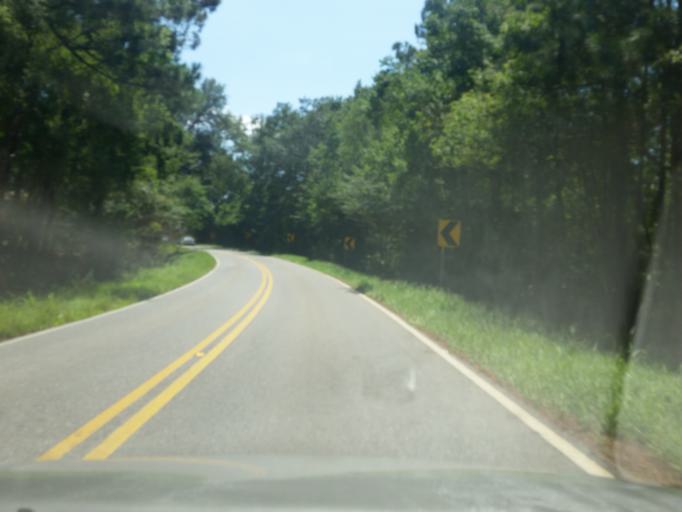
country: US
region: Alabama
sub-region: Baldwin County
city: Robertsdale
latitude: 30.6253
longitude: -87.6651
